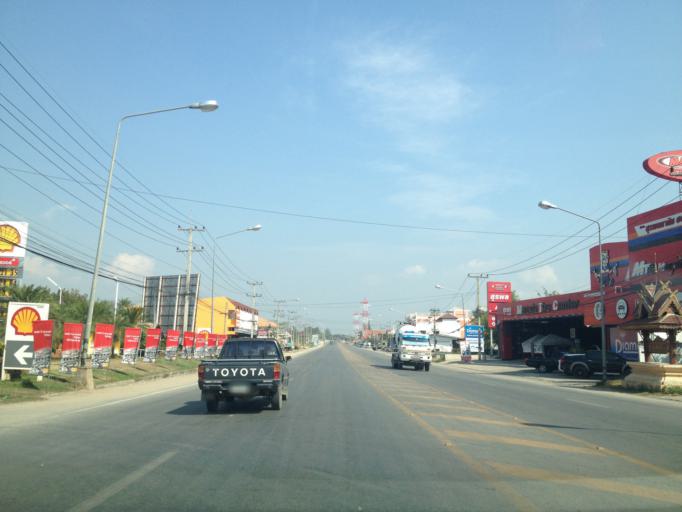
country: TH
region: Chiang Mai
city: Hot
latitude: 18.1981
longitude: 98.6120
